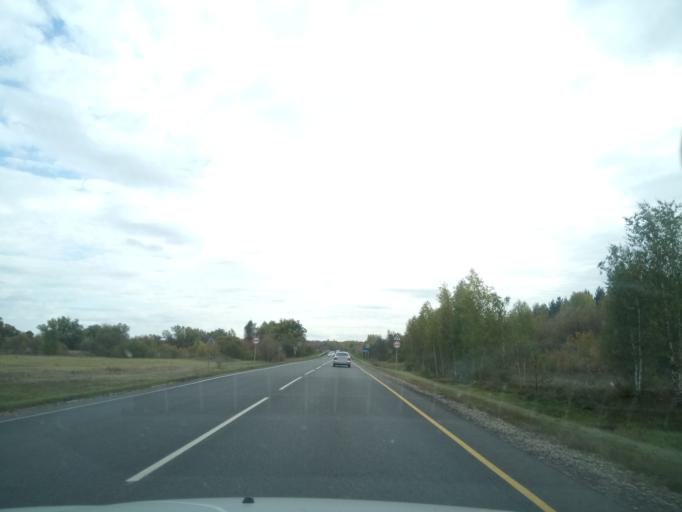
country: RU
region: Nizjnij Novgorod
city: Lukoyanov
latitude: 55.0572
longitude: 44.3667
